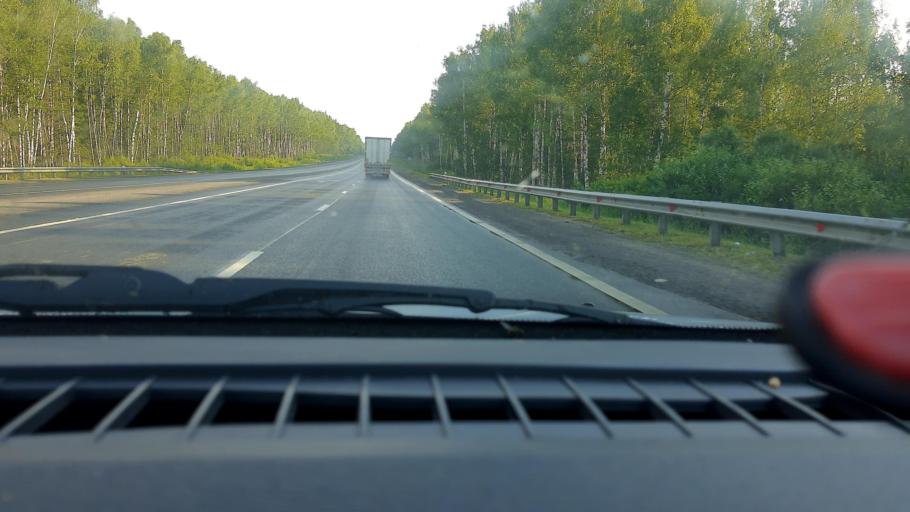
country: RU
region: Nizjnij Novgorod
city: Arzamas
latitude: 55.4975
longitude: 43.8919
